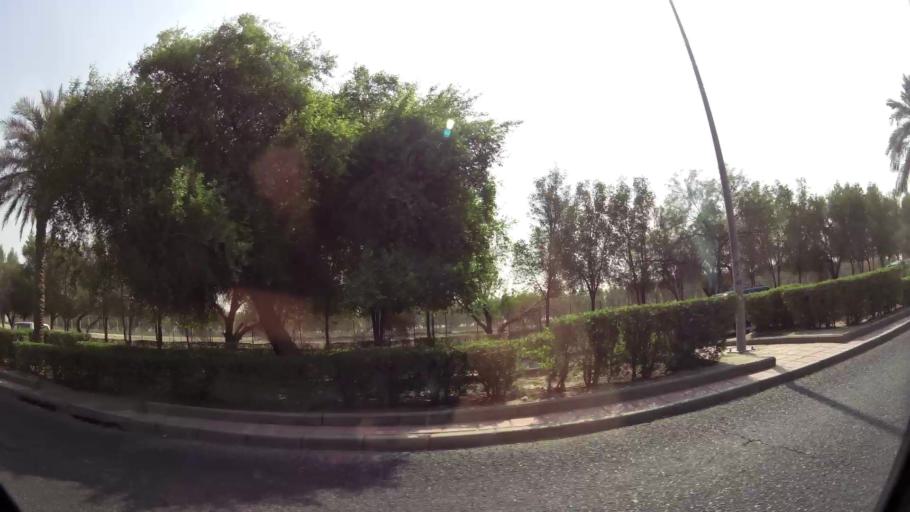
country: KW
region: Al Farwaniyah
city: Al Farwaniyah
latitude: 29.2560
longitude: 47.9508
